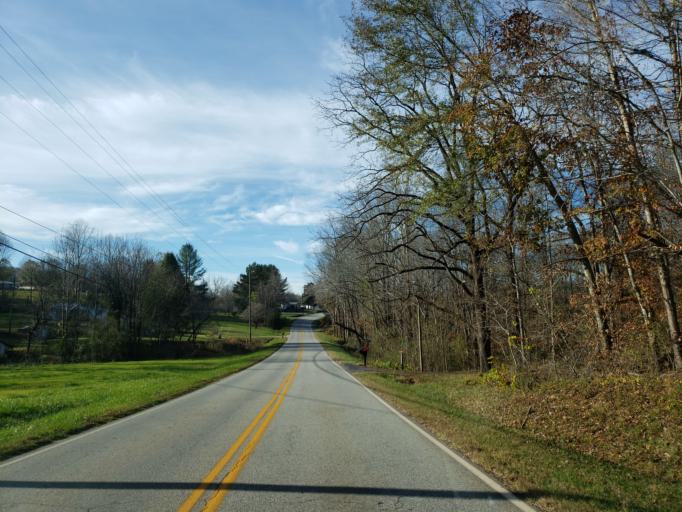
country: US
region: Georgia
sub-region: Lumpkin County
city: Dahlonega
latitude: 34.5649
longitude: -84.0048
